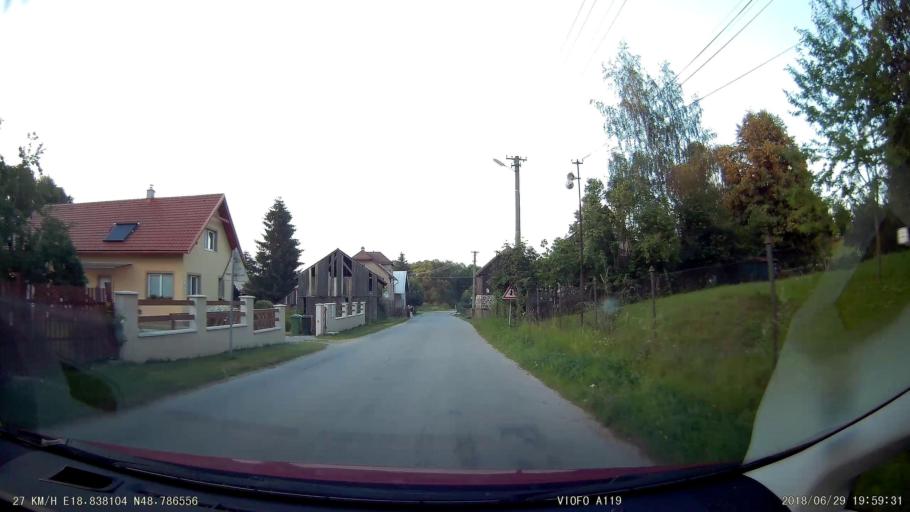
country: SK
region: Nitriansky
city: Handlova
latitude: 48.7866
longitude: 18.8382
